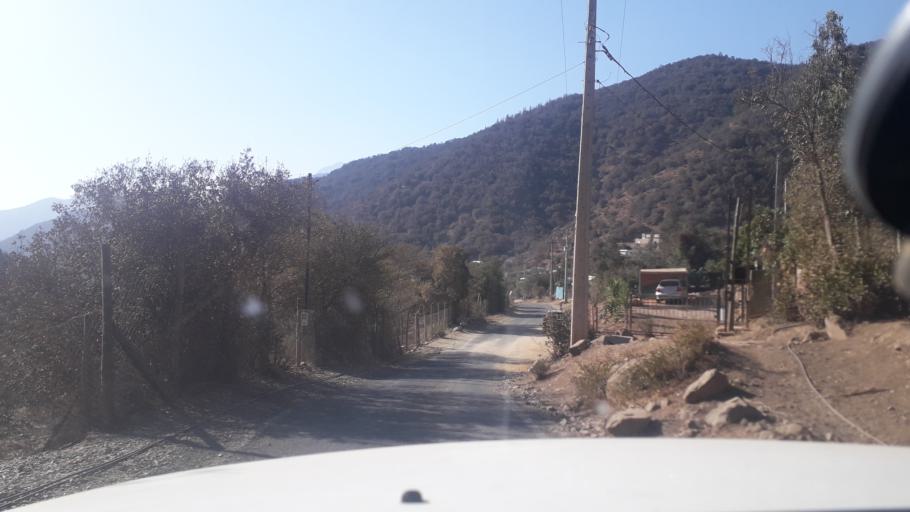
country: CL
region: Valparaiso
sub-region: Provincia de Marga Marga
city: Limache
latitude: -33.0670
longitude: -71.0970
